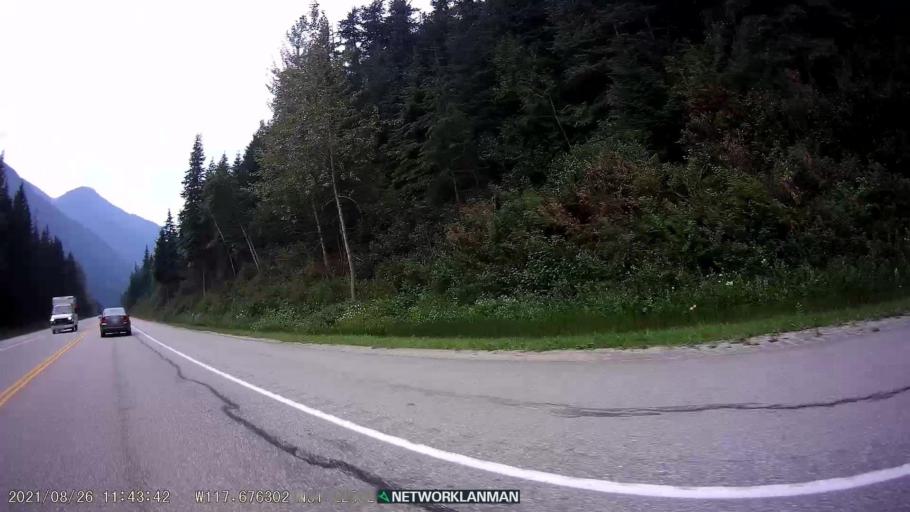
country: CA
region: British Columbia
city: Revelstoke
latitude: 51.2254
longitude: -117.6764
